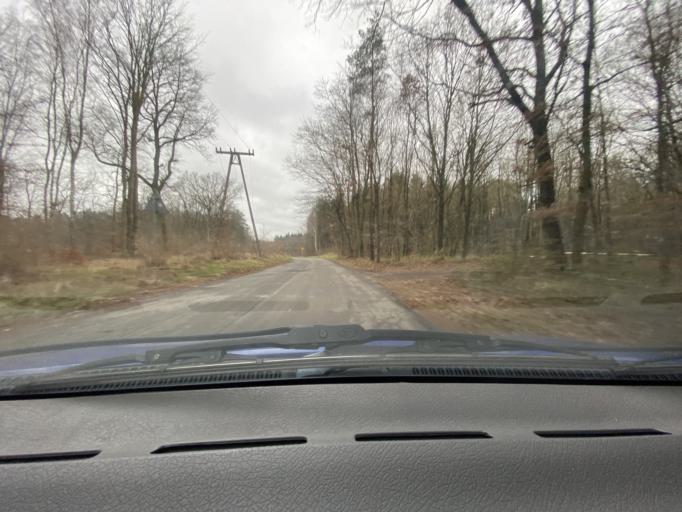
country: PL
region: West Pomeranian Voivodeship
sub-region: Powiat gryficki
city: Gryfice
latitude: 53.9394
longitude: 15.2564
